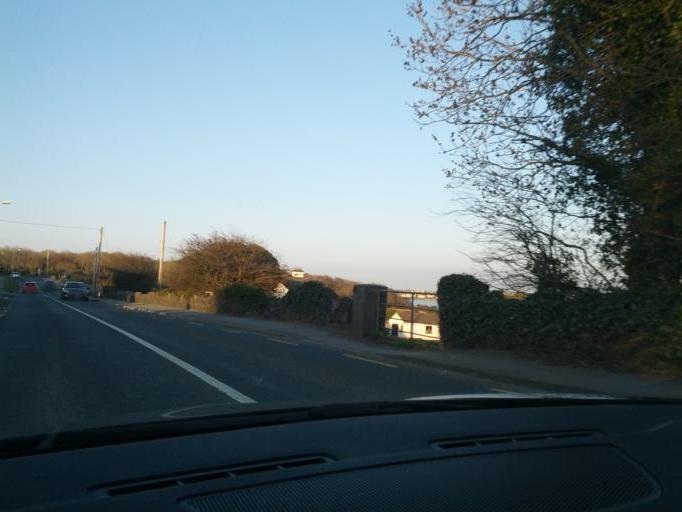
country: IE
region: Connaught
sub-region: County Galway
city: Bearna
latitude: 53.2540
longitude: -9.1355
